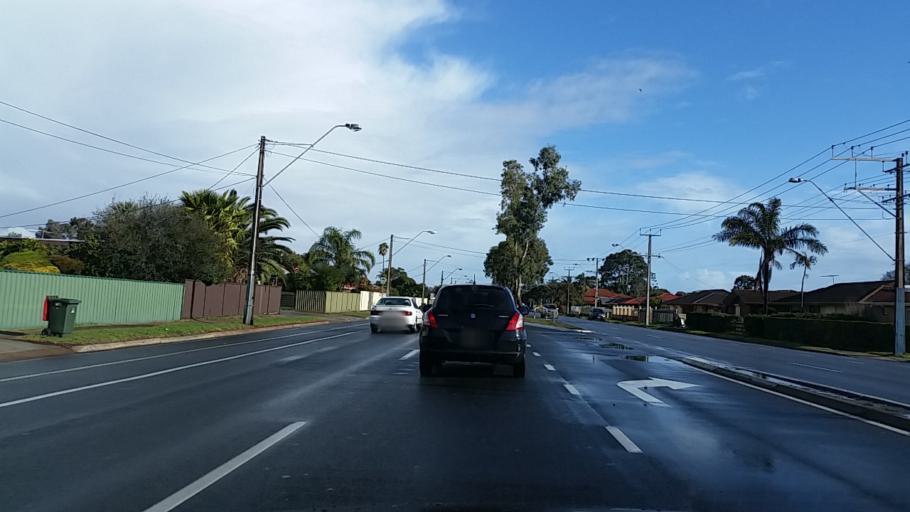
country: AU
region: South Australia
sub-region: Salisbury
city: Salisbury
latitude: -34.7917
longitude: 138.6152
